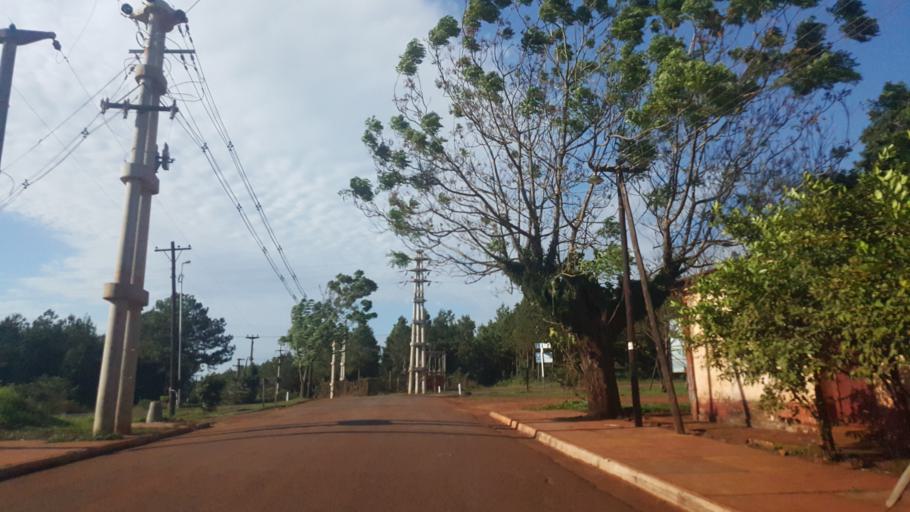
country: AR
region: Misiones
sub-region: Departamento de San Ignacio
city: San Ignacio
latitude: -27.2556
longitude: -55.5267
